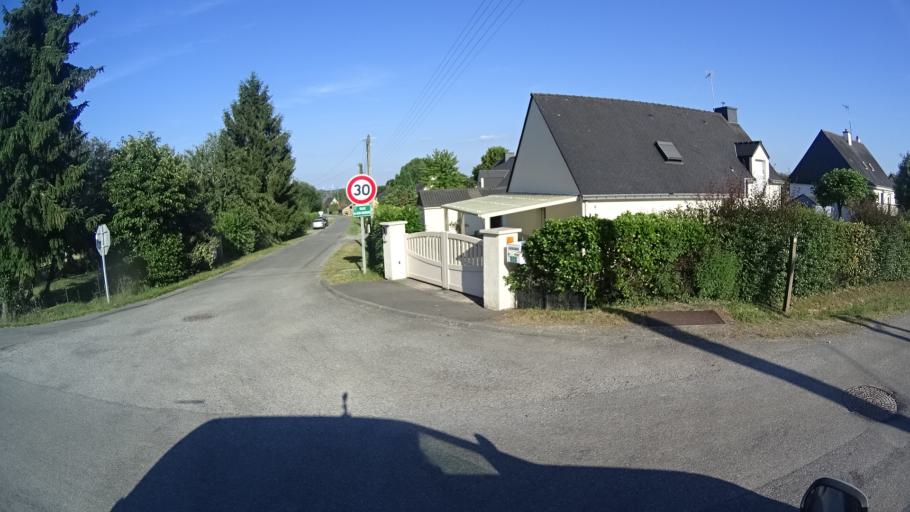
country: FR
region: Brittany
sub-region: Departement du Morbihan
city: Saint-Jean-la-Poterie
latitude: 47.6261
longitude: -2.1066
